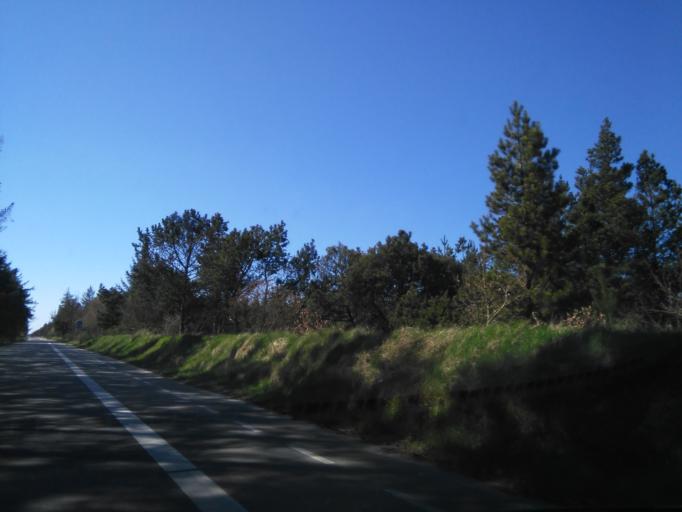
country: DK
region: South Denmark
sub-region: Varde Kommune
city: Oksbol
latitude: 55.5501
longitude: 8.2121
